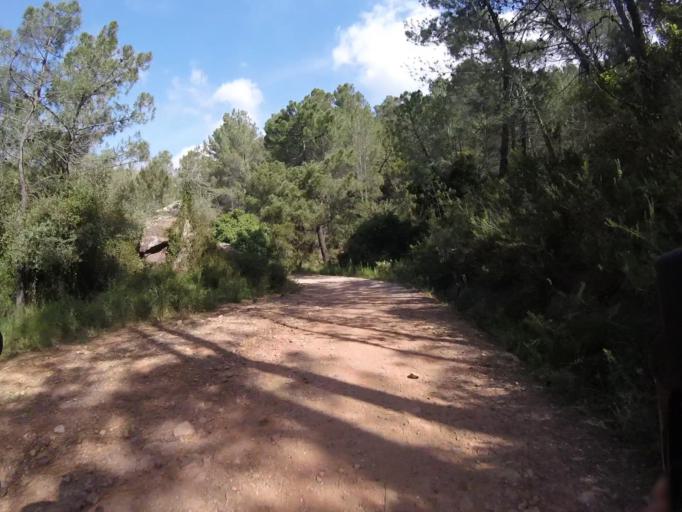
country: ES
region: Valencia
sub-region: Provincia de Castello
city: Benicassim
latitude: 40.0980
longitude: 0.0349
